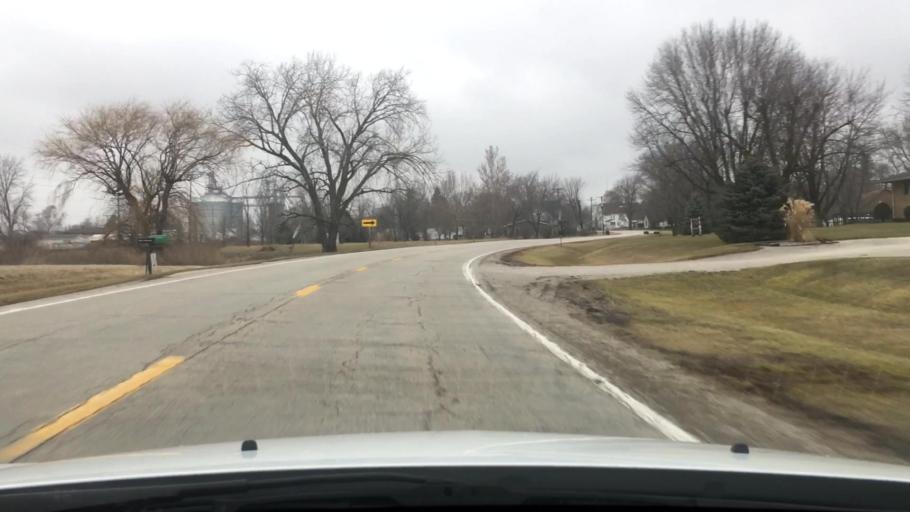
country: US
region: Illinois
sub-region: Iroquois County
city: Sheldon
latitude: 40.8791
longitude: -87.6148
